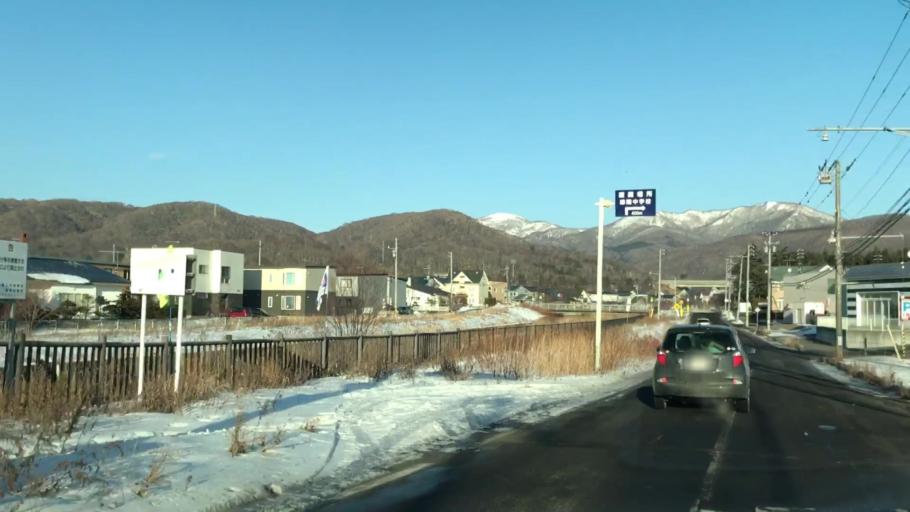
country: JP
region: Hokkaido
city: Muroran
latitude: 42.3851
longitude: 141.0714
